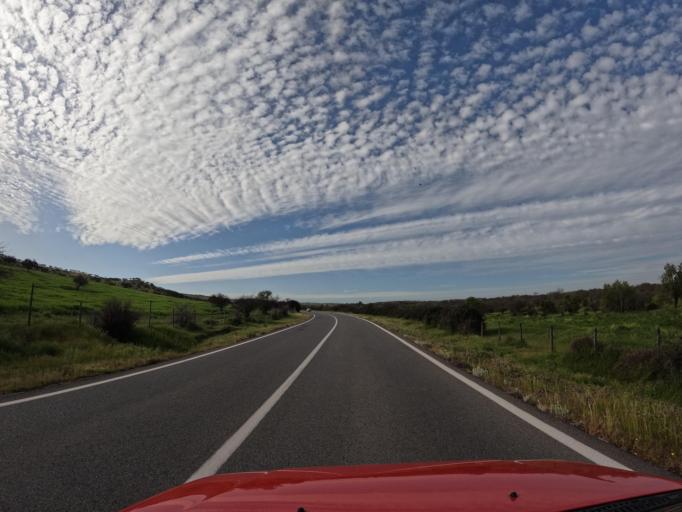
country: CL
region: O'Higgins
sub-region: Provincia de Colchagua
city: Santa Cruz
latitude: -34.2872
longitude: -71.7290
